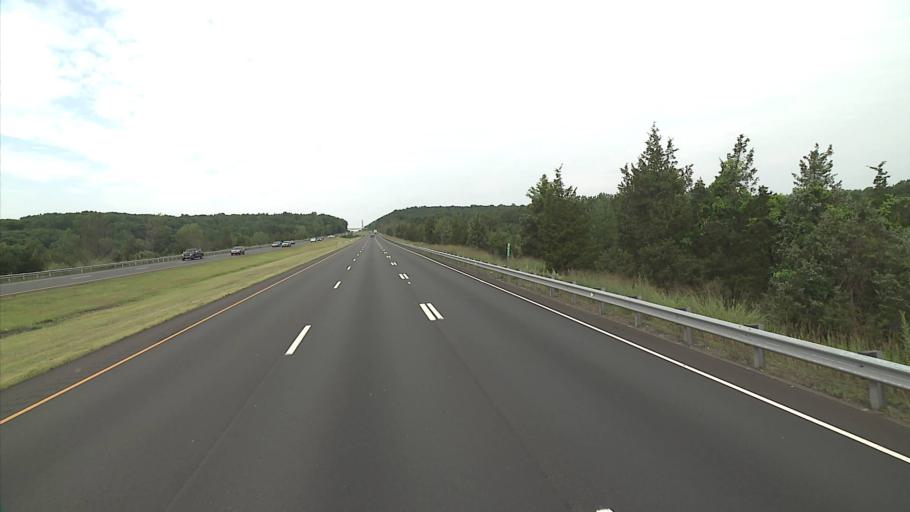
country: US
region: Connecticut
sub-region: New Haven County
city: Middlebury
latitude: 41.5181
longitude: -73.1061
